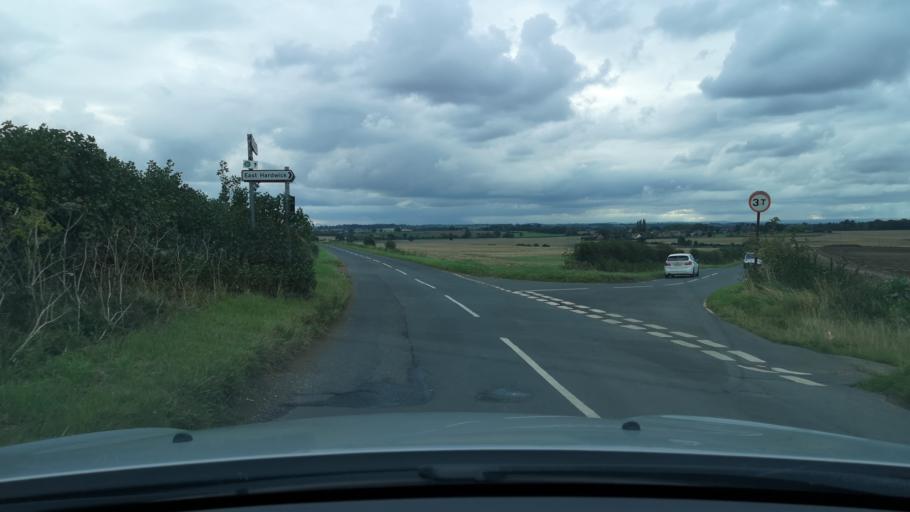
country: GB
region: England
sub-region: City and Borough of Wakefield
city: Darrington
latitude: 53.6707
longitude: -1.2876
